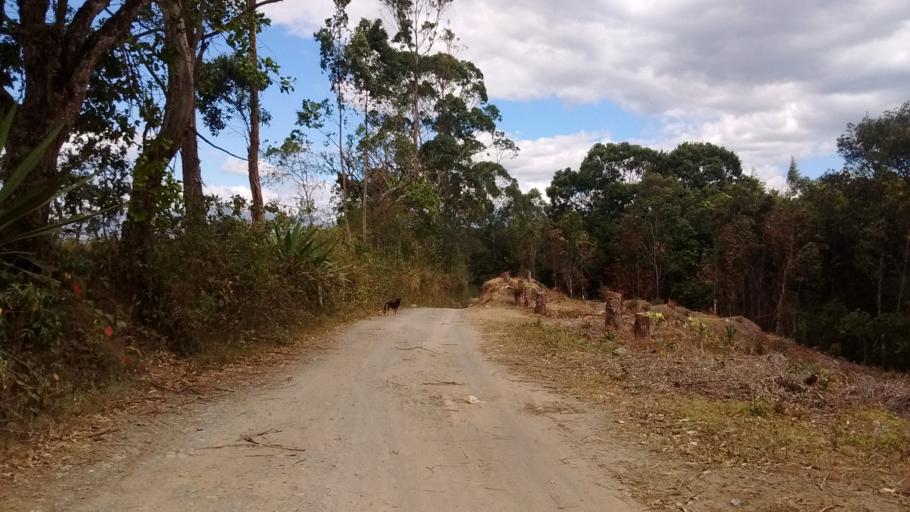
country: CO
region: Cauca
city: Popayan
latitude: 2.4939
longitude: -76.5886
